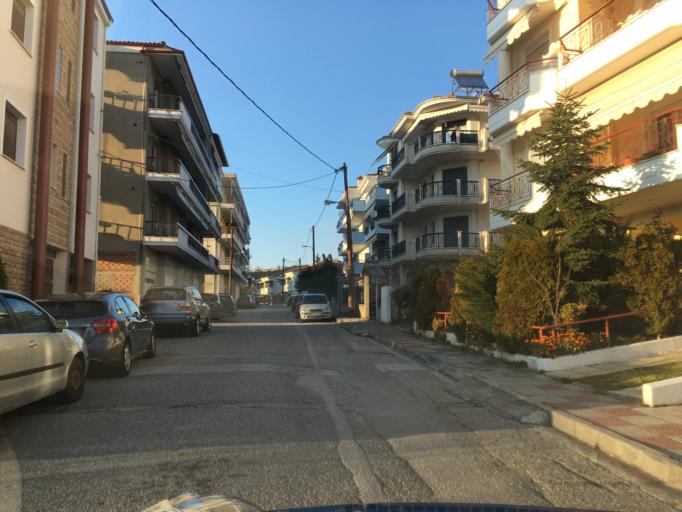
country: GR
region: West Macedonia
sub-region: Nomos Kozanis
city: Kozani
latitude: 40.2948
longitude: 21.7970
